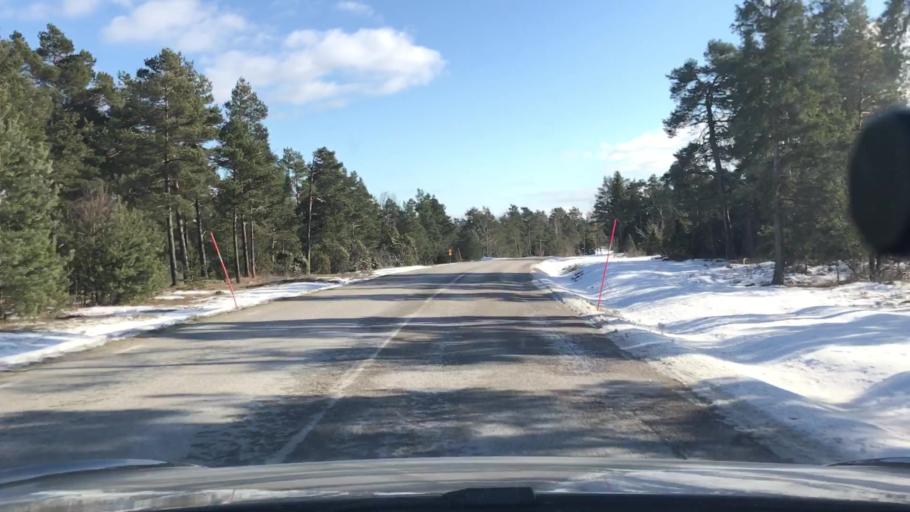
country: SE
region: Gotland
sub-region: Gotland
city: Hemse
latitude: 57.3471
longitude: 18.6917
